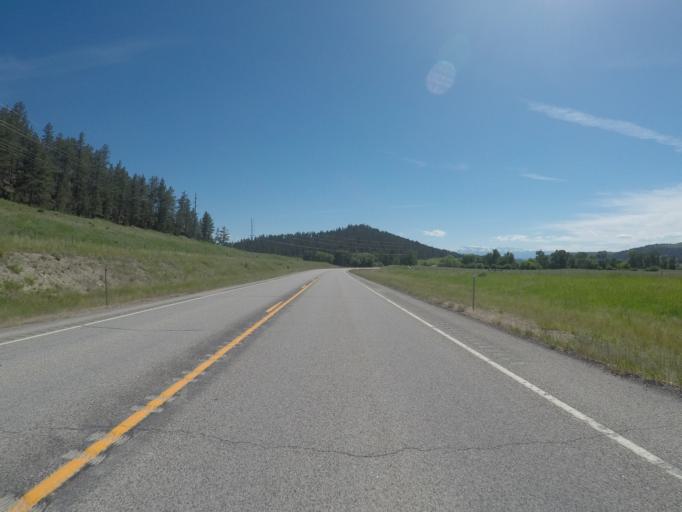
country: US
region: Montana
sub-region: Stillwater County
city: Columbus
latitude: 45.5968
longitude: -109.2939
